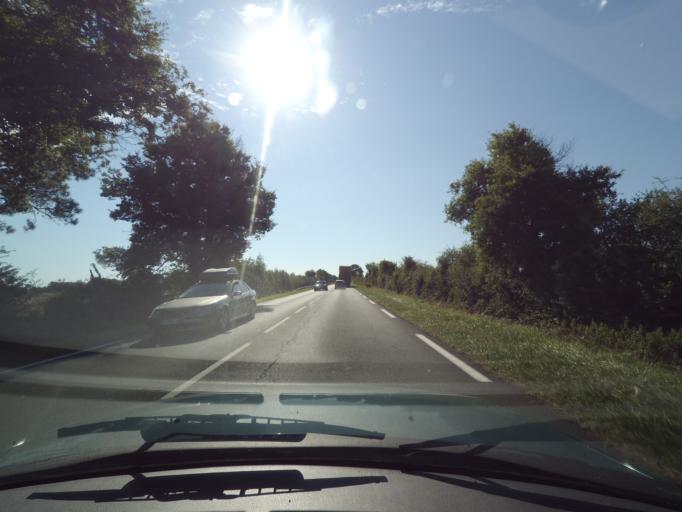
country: FR
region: Poitou-Charentes
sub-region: Departement de la Vienne
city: Lussac-les-Chateaux
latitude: 46.4190
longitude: 0.6429
